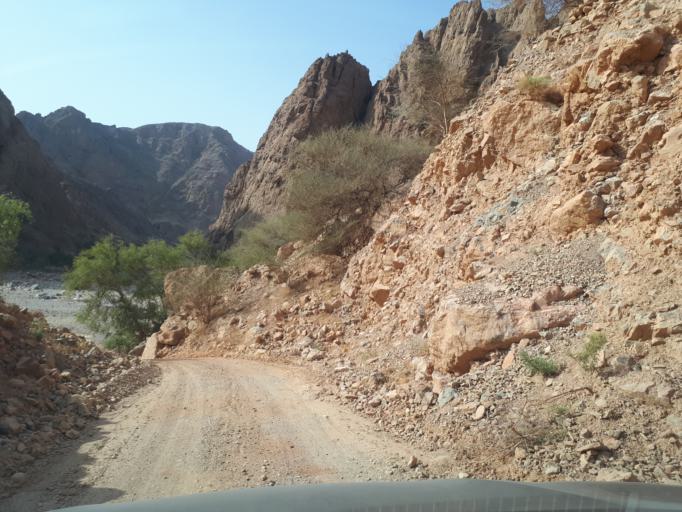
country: OM
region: Ash Sharqiyah
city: Al Qabil
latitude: 23.0618
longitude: 58.9877
